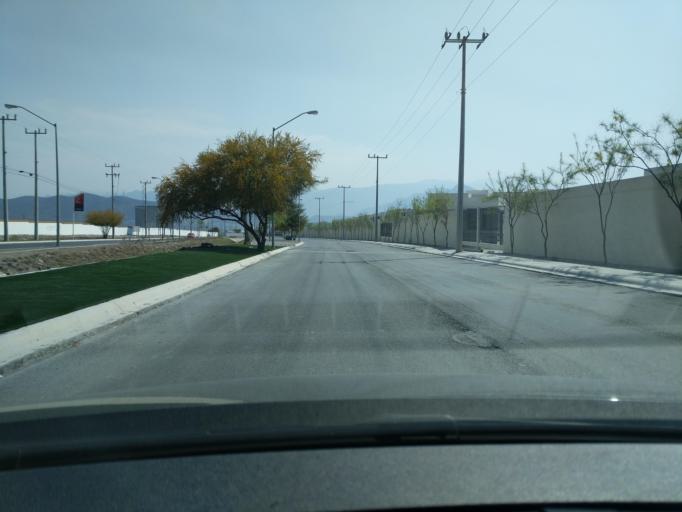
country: MX
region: Nuevo Leon
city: Garcia
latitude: 25.8115
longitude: -100.5379
